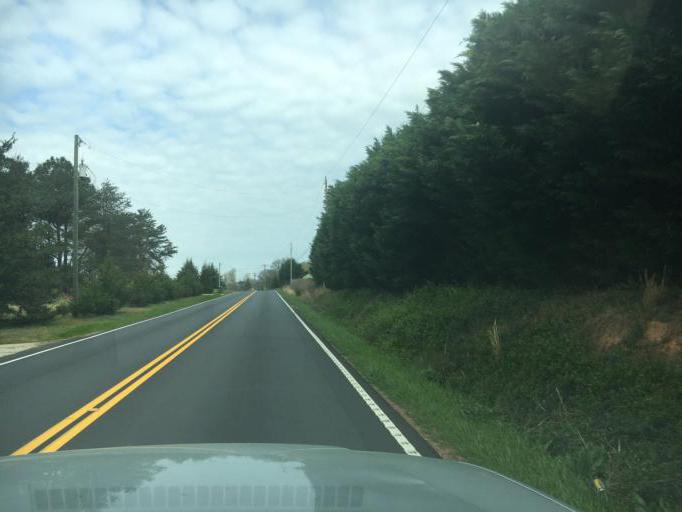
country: US
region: South Carolina
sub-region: Spartanburg County
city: Inman
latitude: 35.0189
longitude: -82.0808
